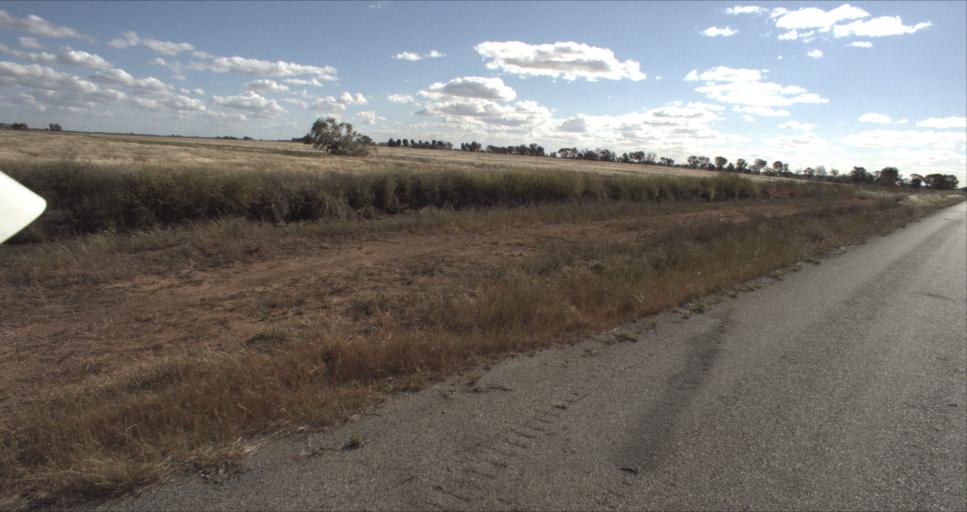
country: AU
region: New South Wales
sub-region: Leeton
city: Leeton
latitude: -34.4414
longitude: 146.2329
